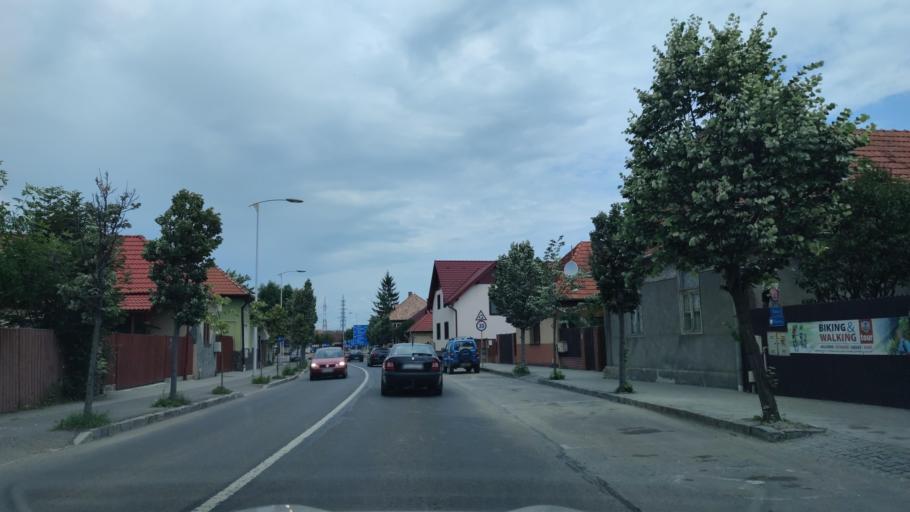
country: RO
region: Harghita
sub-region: Municipiul Miercurea Ciuc
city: Miercurea-Ciuc
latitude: 46.3796
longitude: 25.8016
